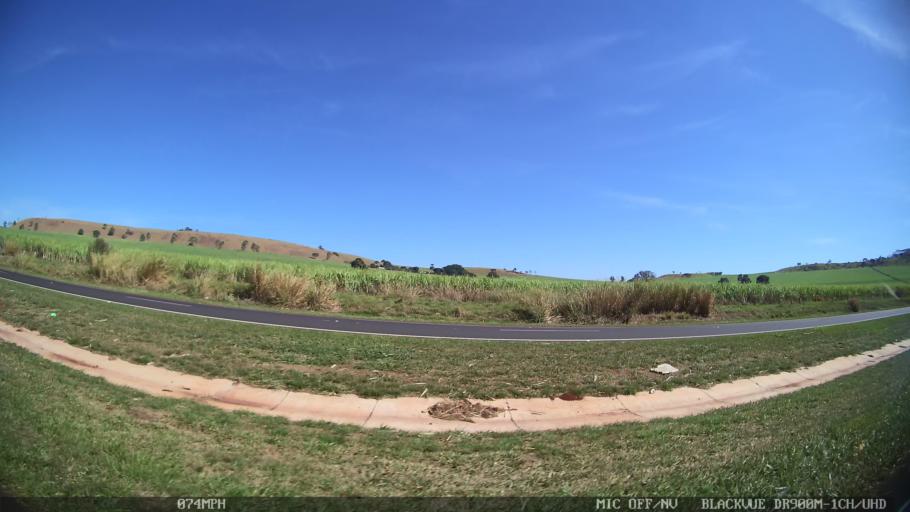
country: BR
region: Sao Paulo
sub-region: Sao Simao
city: Sao Simao
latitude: -21.4391
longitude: -47.6504
